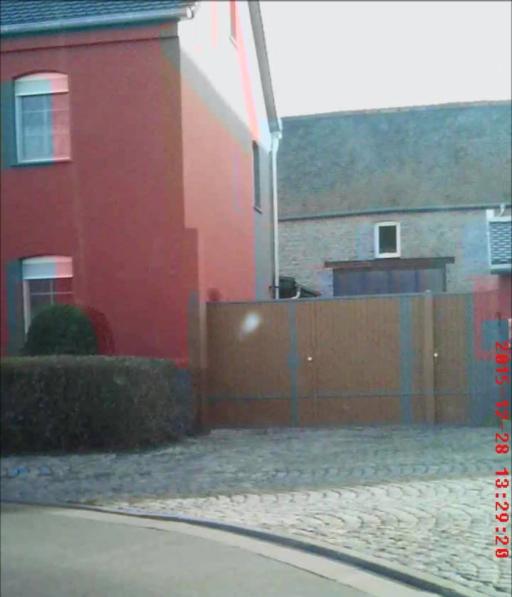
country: DE
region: Thuringia
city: Eberstedt
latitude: 51.0715
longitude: 11.5862
